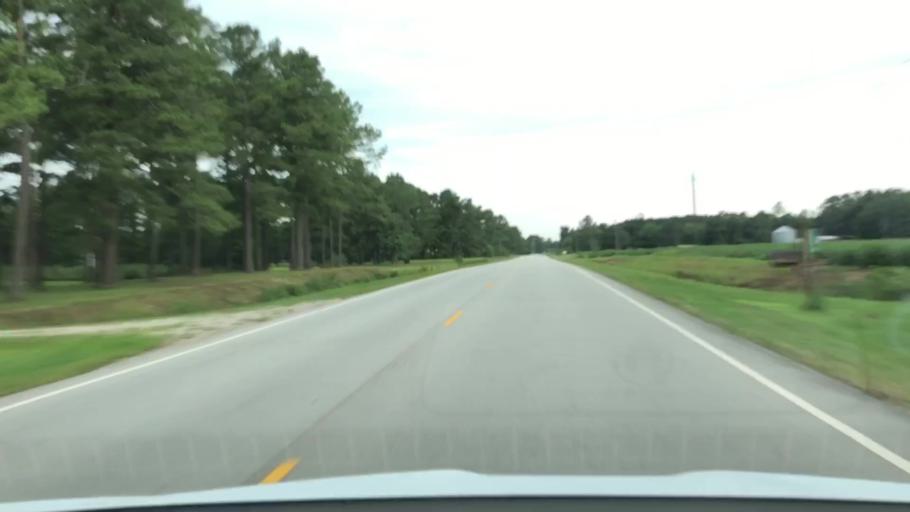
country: US
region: North Carolina
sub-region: Jones County
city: Trenton
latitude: 35.0137
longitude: -77.2934
